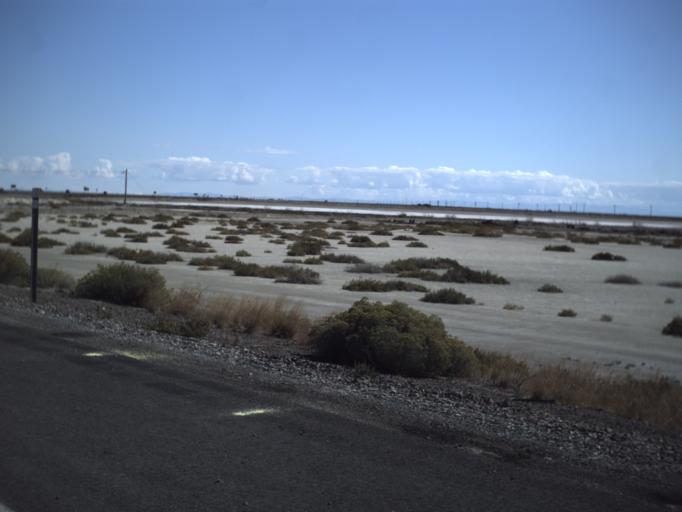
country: US
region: Utah
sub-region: Tooele County
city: Wendover
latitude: 40.7400
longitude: -113.9691
